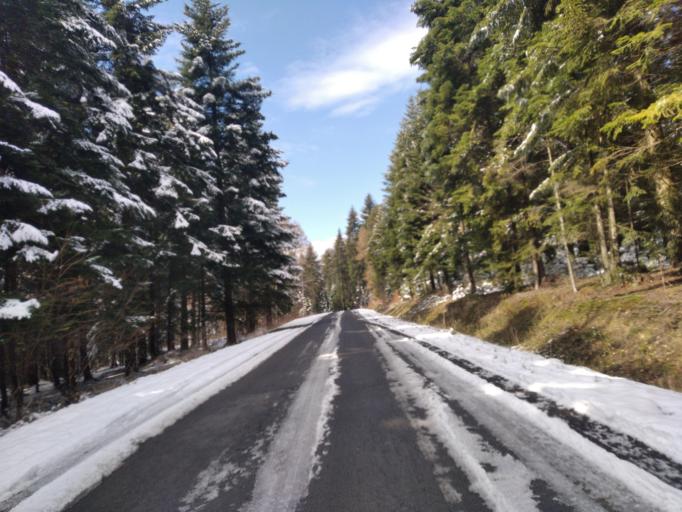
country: PL
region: Subcarpathian Voivodeship
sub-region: Powiat ropczycko-sedziszowski
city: Ropczyce
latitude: 50.0154
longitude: 21.6044
